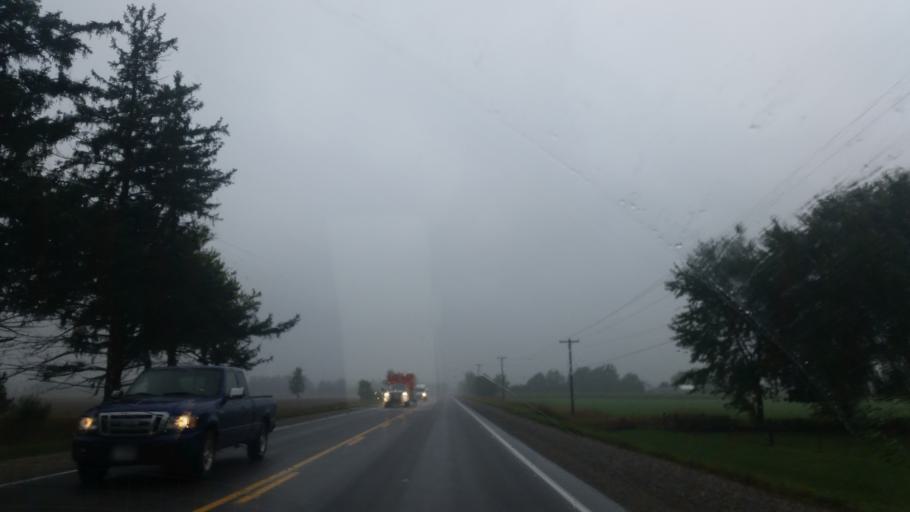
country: CA
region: Ontario
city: Stratford
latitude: 43.3031
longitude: -81.0402
